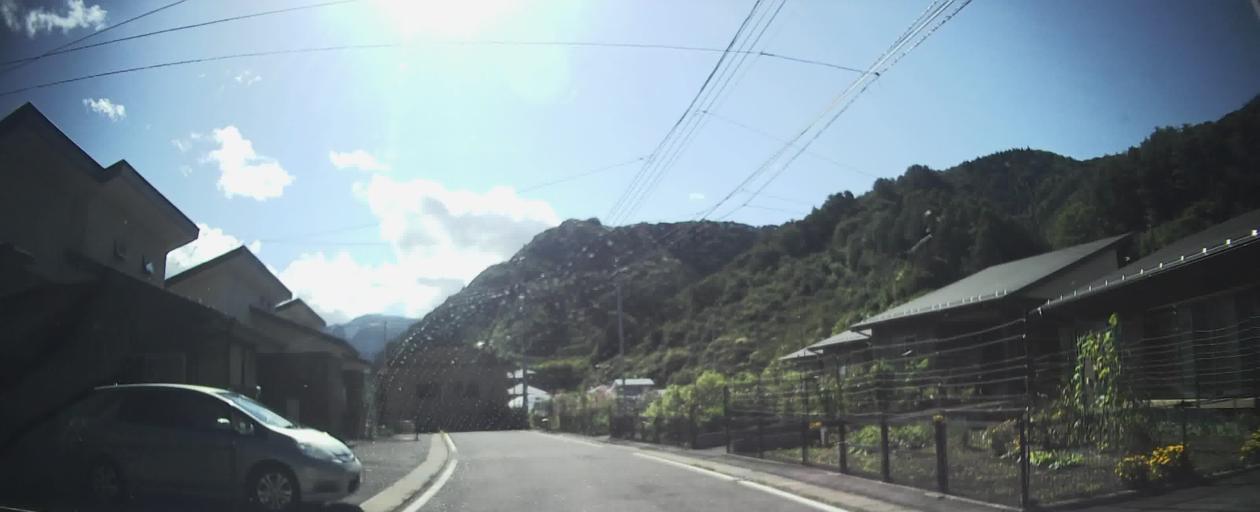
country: JP
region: Gunma
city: Nakanojomachi
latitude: 36.5567
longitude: 138.7035
